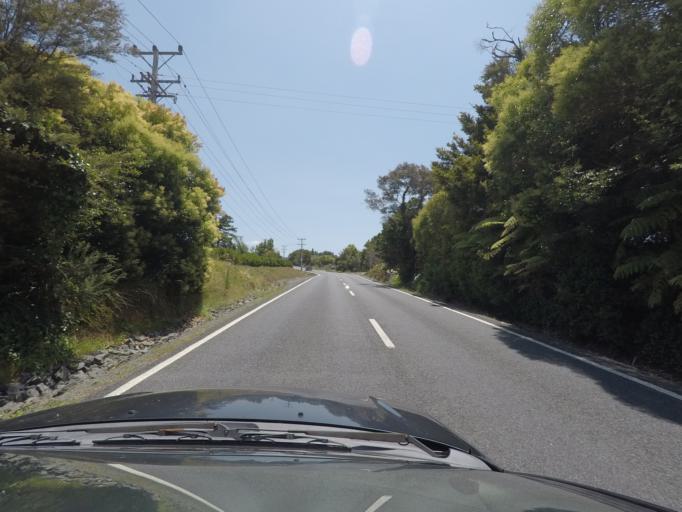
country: NZ
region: Auckland
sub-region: Auckland
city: Warkworth
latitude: -36.3904
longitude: 174.6605
